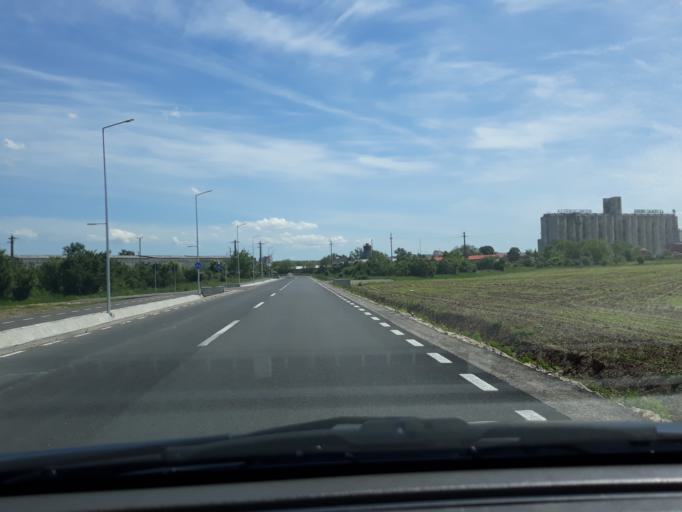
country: RO
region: Bihor
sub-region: Comuna Santandrei
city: Santandrei
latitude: 47.0669
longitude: 21.8854
